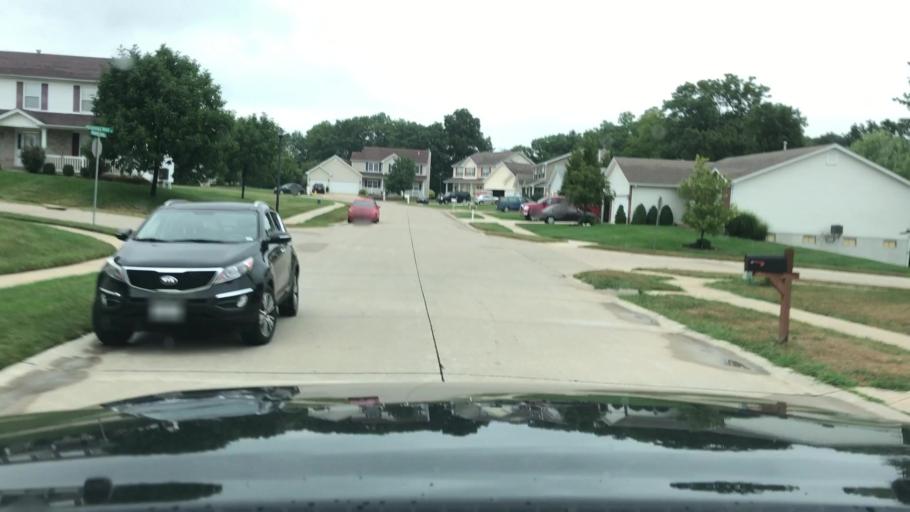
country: US
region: Missouri
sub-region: Saint Charles County
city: Wentzville
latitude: 38.8379
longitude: -90.8835
